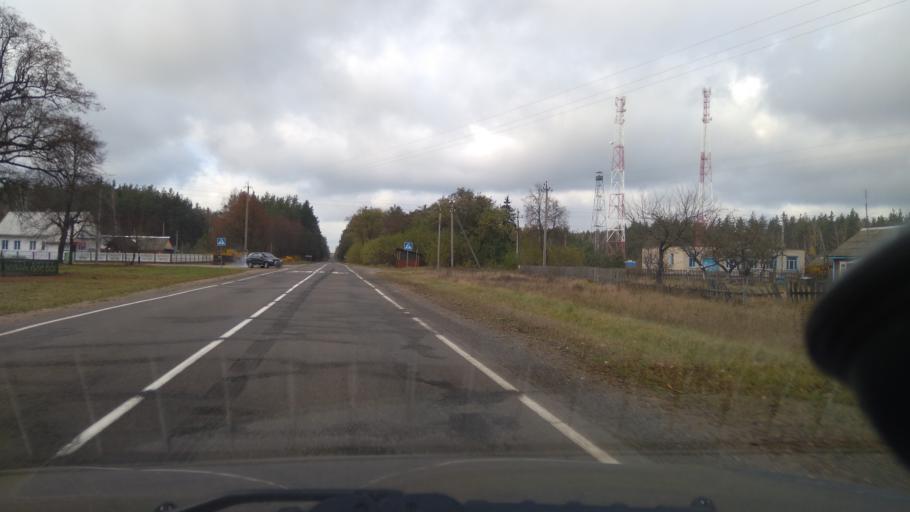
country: BY
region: Minsk
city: Slutsk
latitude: 53.2088
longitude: 27.7637
